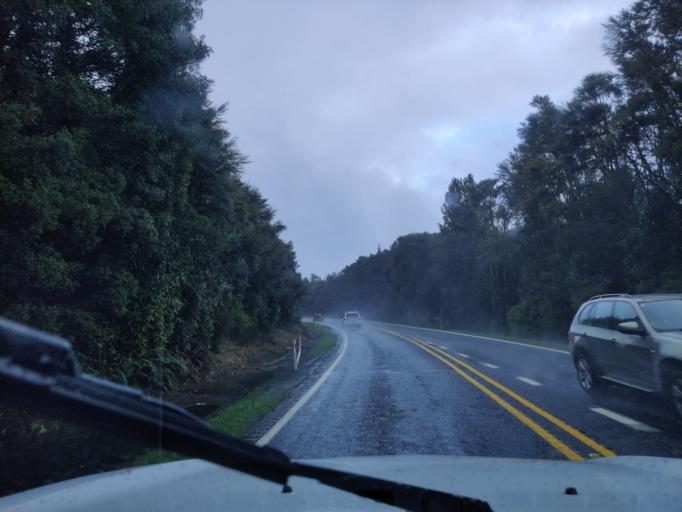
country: NZ
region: Waikato
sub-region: South Waikato District
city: Tokoroa
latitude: -38.0218
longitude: 175.9569
